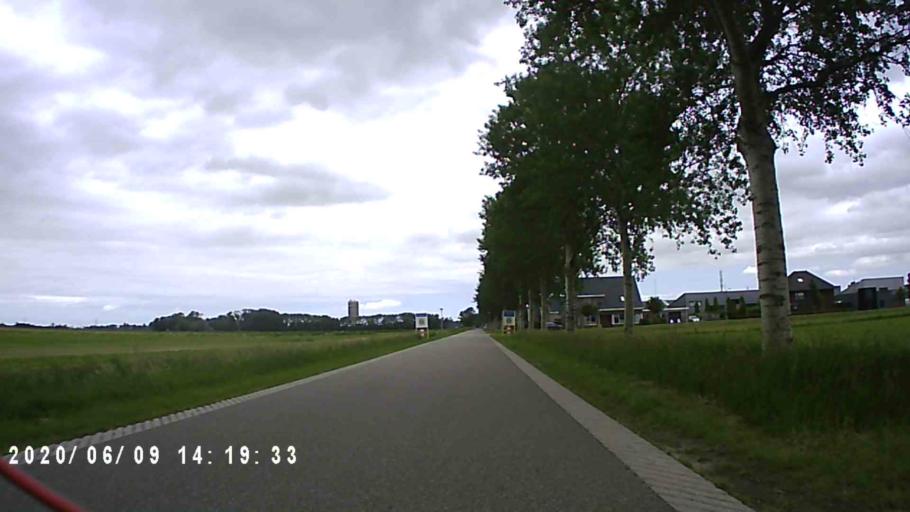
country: NL
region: Groningen
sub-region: Gemeente Bedum
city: Bedum
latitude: 53.2909
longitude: 6.5921
